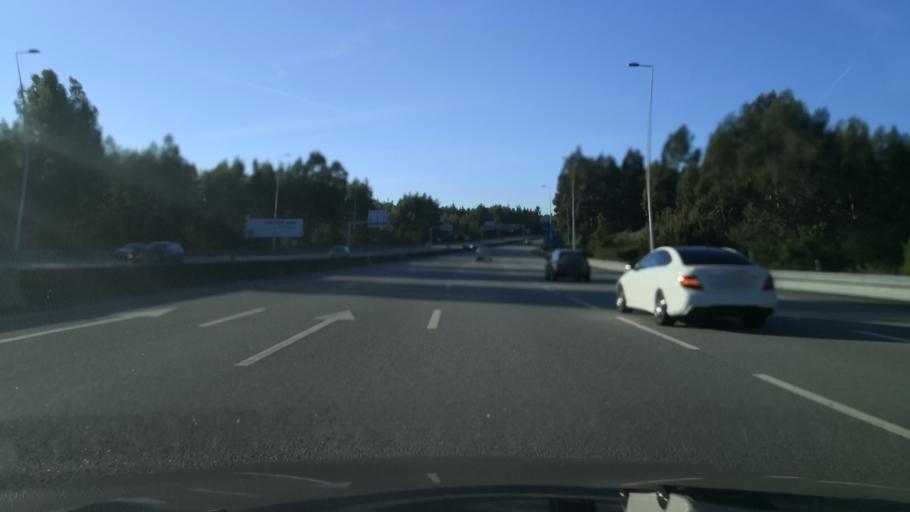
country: PT
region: Porto
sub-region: Maia
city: Nogueira
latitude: 41.2470
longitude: -8.5667
